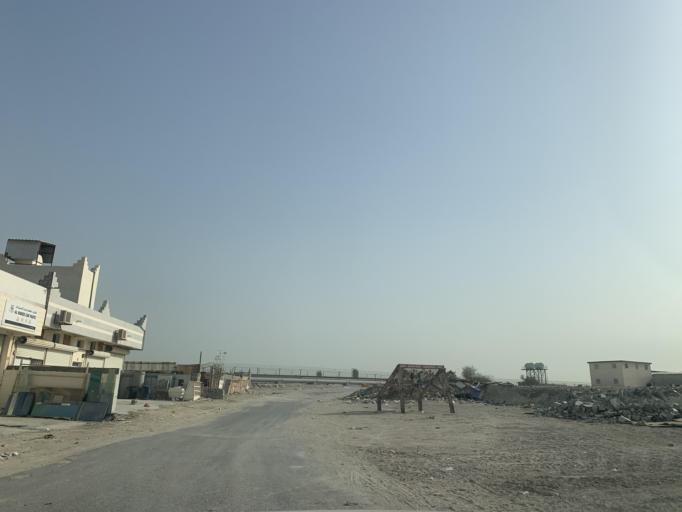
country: BH
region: Central Governorate
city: Madinat Hamad
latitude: 26.1445
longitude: 50.4815
